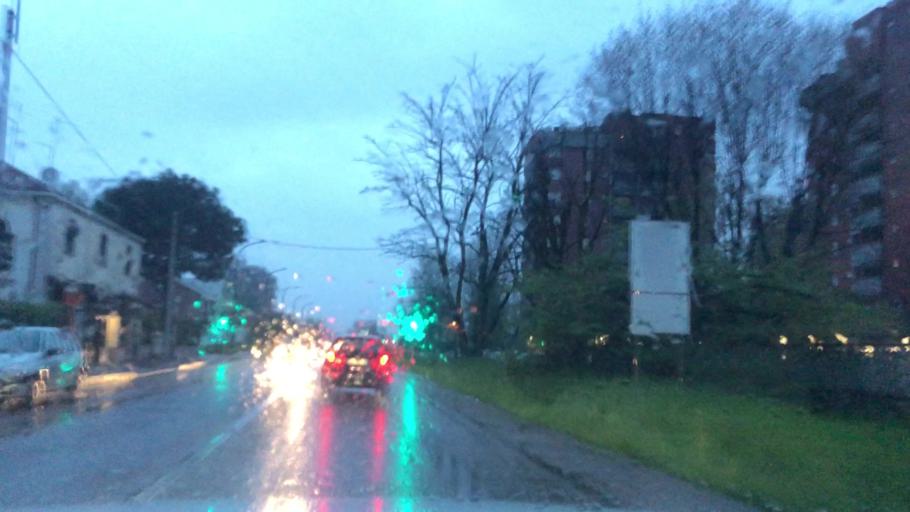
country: IT
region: Lombardy
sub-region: Citta metropolitana di Milano
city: Cusano Milanino
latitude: 45.5561
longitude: 9.1861
